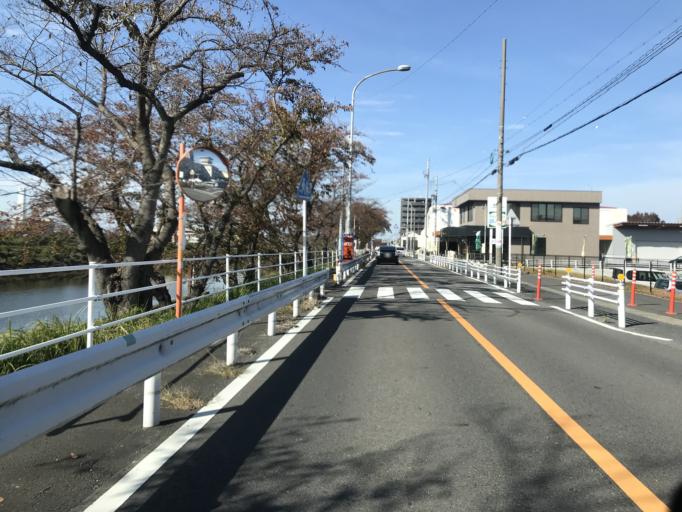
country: JP
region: Aichi
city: Iwakura
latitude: 35.2371
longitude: 136.8413
